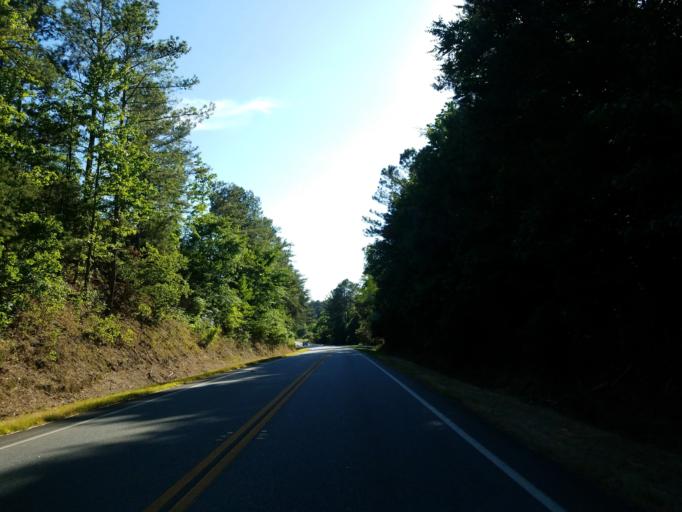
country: US
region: Georgia
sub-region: Gordon County
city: Calhoun
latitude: 34.5744
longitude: -84.9644
